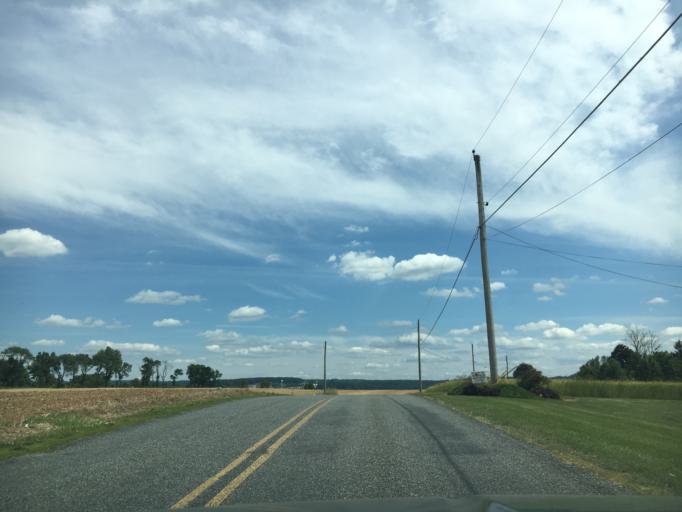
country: US
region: Pennsylvania
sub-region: Berks County
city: Kutztown
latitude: 40.4989
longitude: -75.7890
